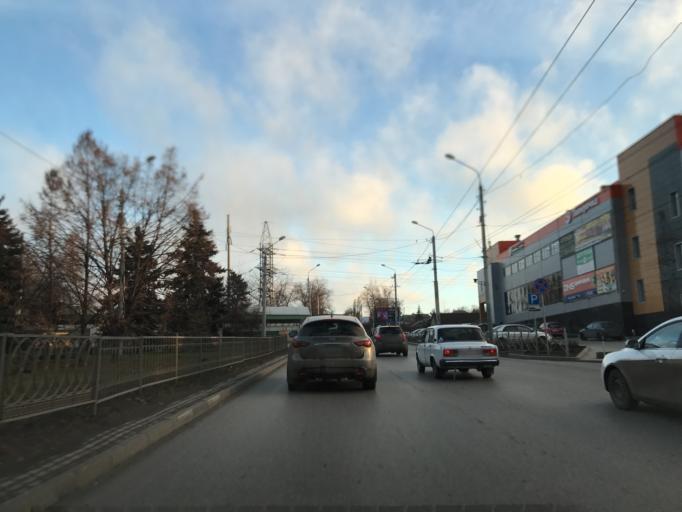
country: RU
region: Rostov
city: Severnyy
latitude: 47.2599
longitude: 39.6894
